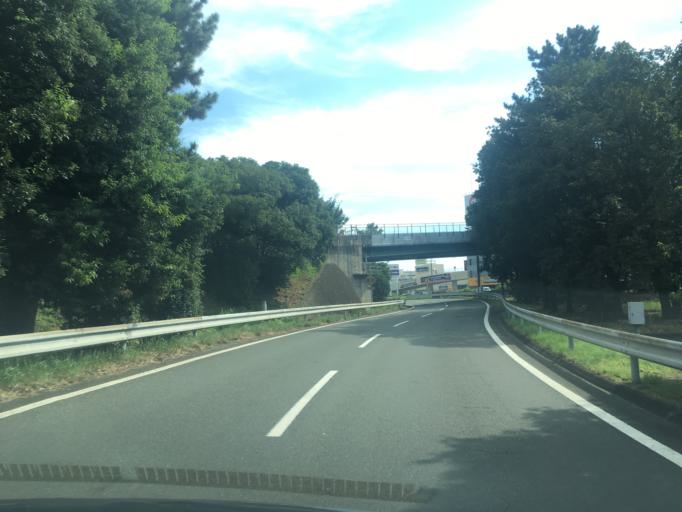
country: JP
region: Gunma
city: Maebashi-shi
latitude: 36.3762
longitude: 139.0312
